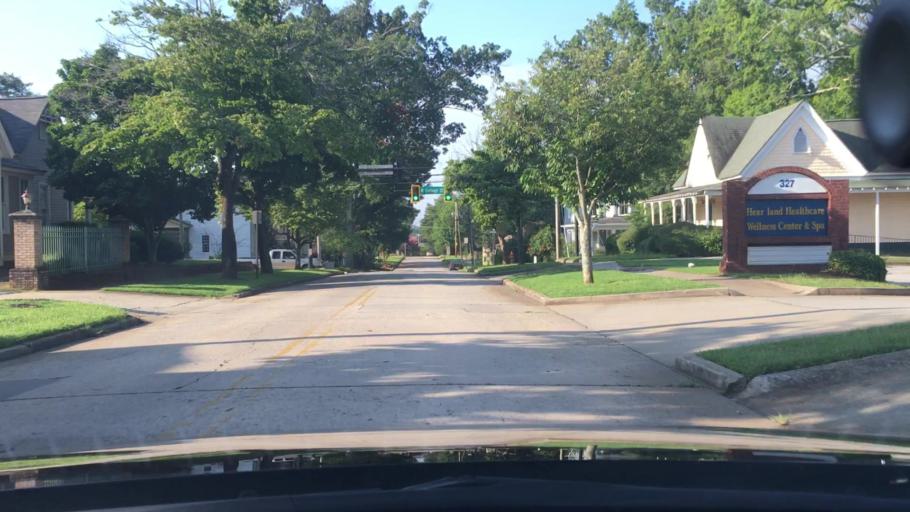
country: US
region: Georgia
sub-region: Spalding County
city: Griffin
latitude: 33.2450
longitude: -84.2672
